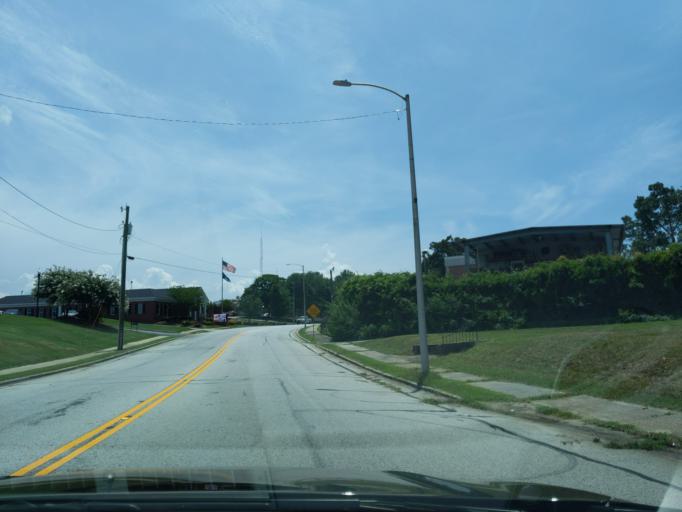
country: US
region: South Carolina
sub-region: Laurens County
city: Laurens
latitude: 34.5010
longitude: -82.0199
